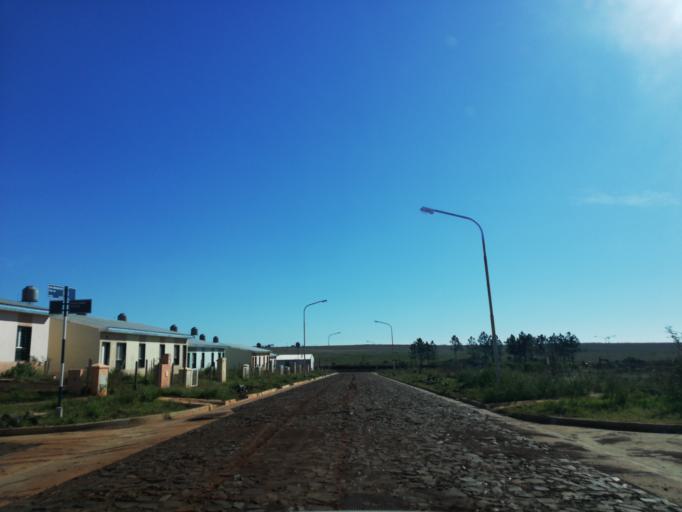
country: AR
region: Misiones
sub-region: Departamento de Capital
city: Posadas
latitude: -27.4069
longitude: -55.9946
